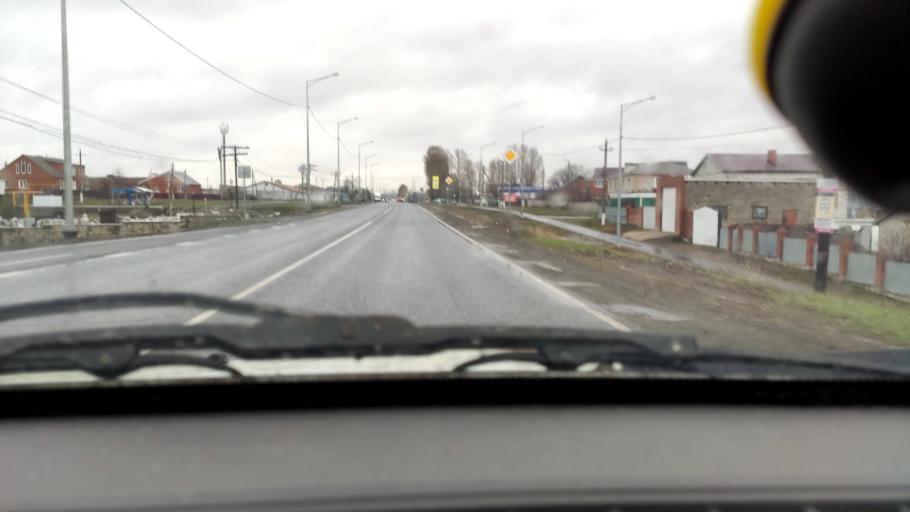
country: RU
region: Samara
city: Zhigulevsk
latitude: 53.5479
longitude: 49.5217
